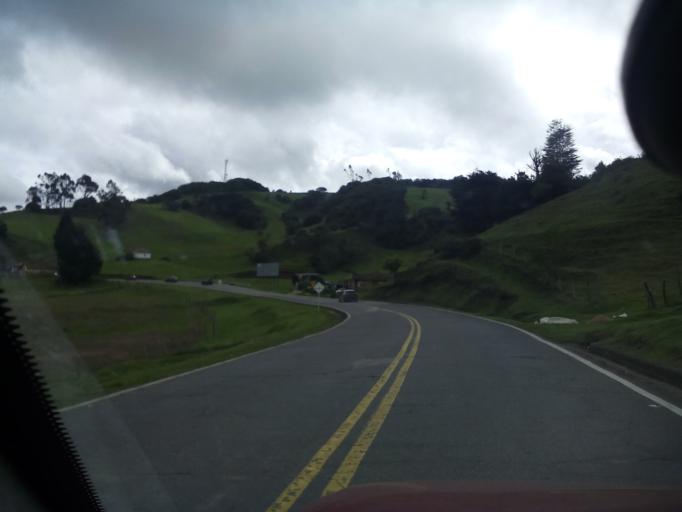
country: CO
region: Boyaca
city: Combita
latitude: 5.6605
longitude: -73.3590
